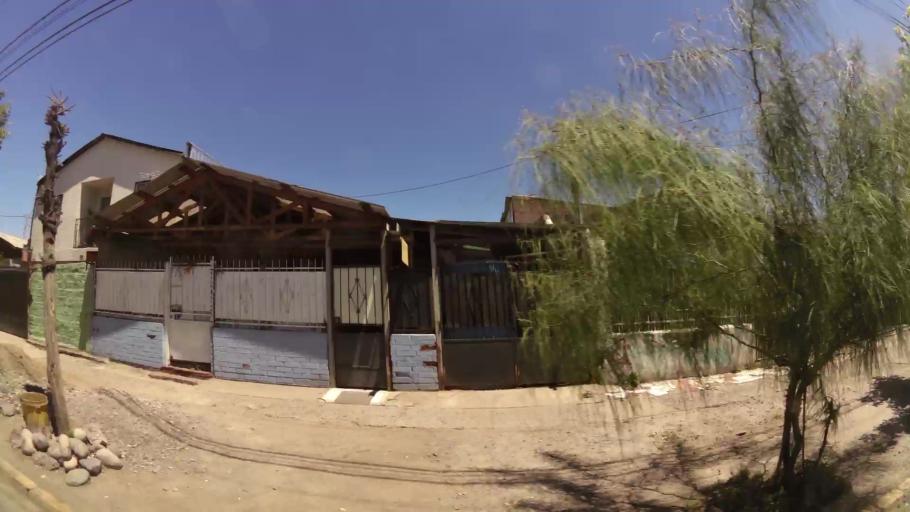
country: CL
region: Santiago Metropolitan
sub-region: Provincia de Santiago
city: La Pintana
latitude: -33.5693
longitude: -70.6588
